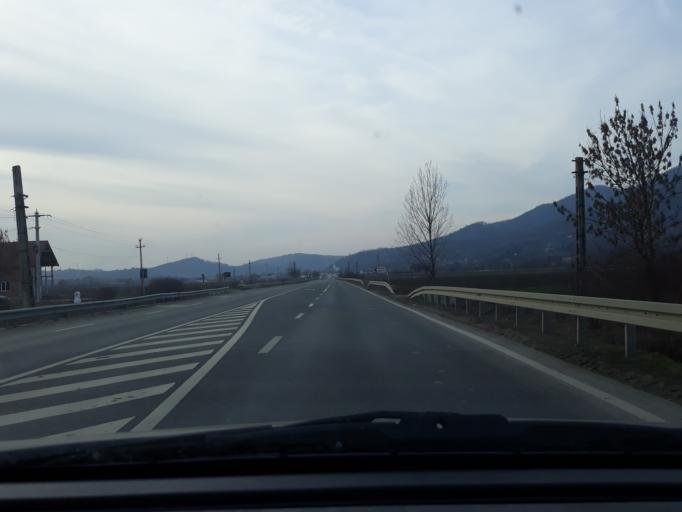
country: RO
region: Salaj
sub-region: Oras Simleu Silvaniei
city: Simleu Silvaniei
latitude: 47.2292
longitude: 22.8350
